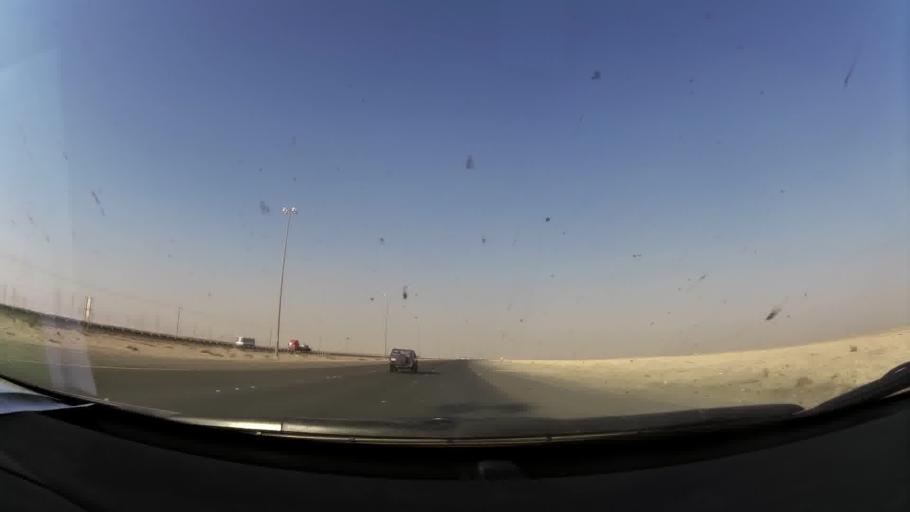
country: KW
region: Muhafazat al Jahra'
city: Al Jahra'
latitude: 29.6287
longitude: 47.6635
